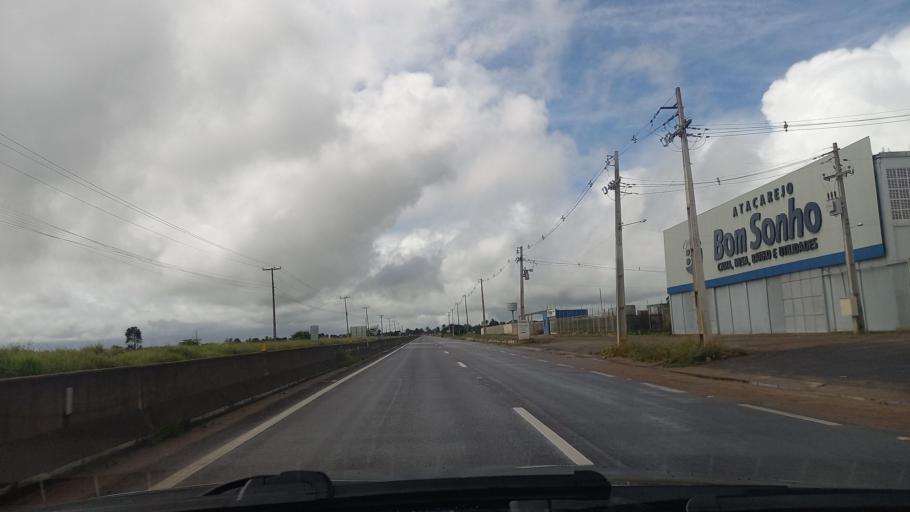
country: BR
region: Alagoas
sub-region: Limoeiro De Anadia
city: Limoeiro de Anadia
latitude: -9.7616
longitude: -36.5414
